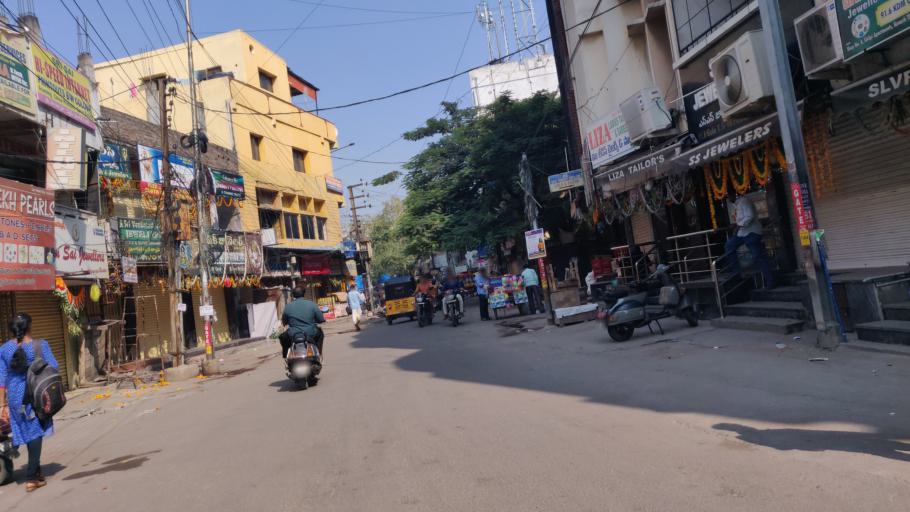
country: IN
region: Telangana
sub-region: Rangareddi
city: Gaddi Annaram
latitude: 17.3670
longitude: 78.5251
